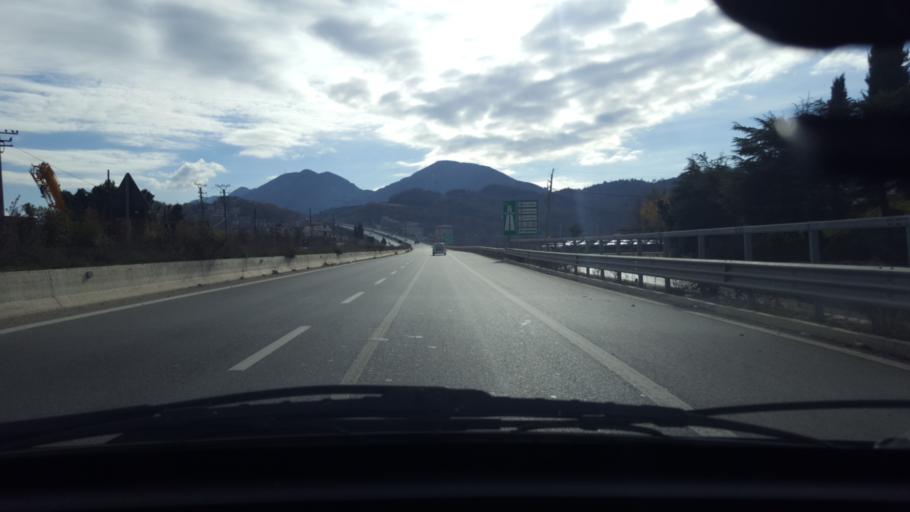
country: AL
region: Tirane
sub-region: Rrethi i Tiranes
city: Petrele
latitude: 41.2795
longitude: 19.8546
